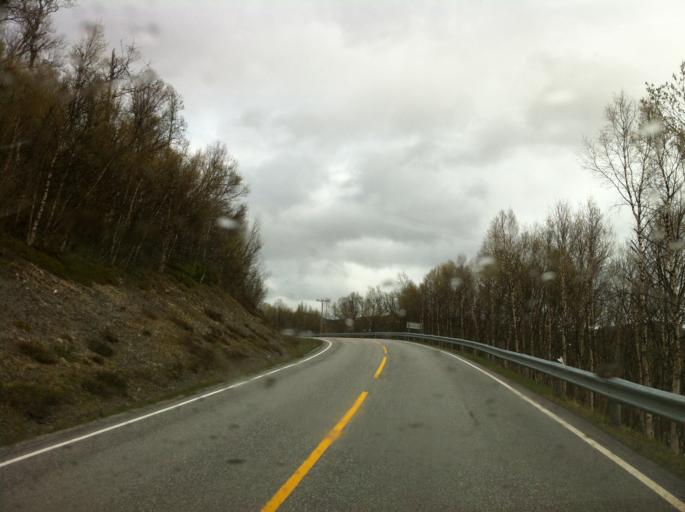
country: NO
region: Sor-Trondelag
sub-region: Roros
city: Roros
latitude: 62.5974
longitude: 11.6986
